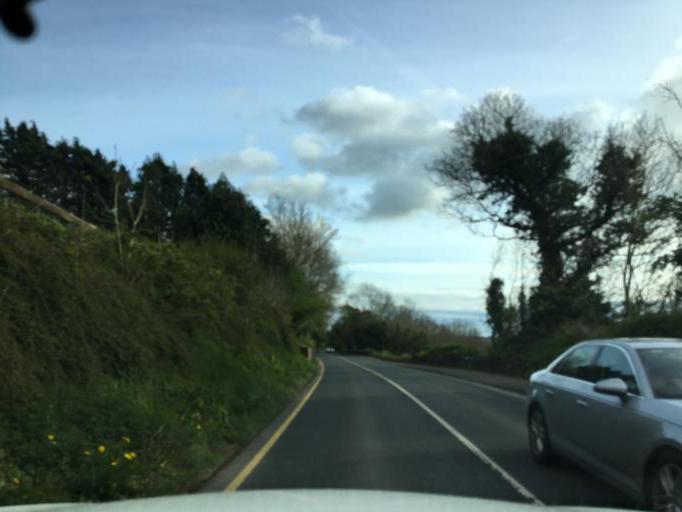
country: IE
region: Leinster
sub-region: Loch Garman
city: New Ross
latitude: 52.4100
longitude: -6.9381
